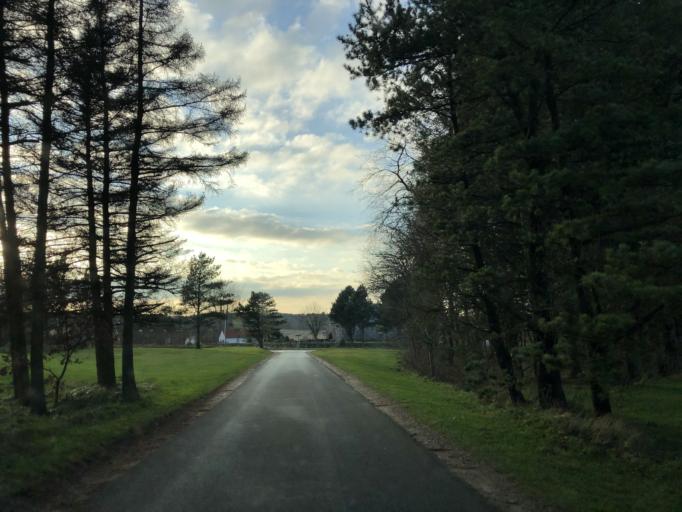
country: DK
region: Central Jutland
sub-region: Holstebro Kommune
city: Ulfborg
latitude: 56.3203
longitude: 8.4244
